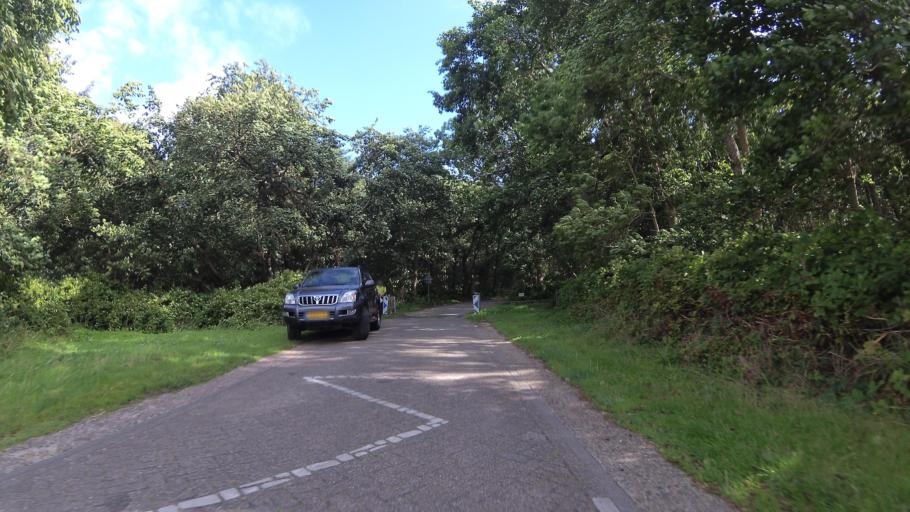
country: NL
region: North Holland
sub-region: Gemeente Texel
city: Den Burg
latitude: 53.0690
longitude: 4.7507
